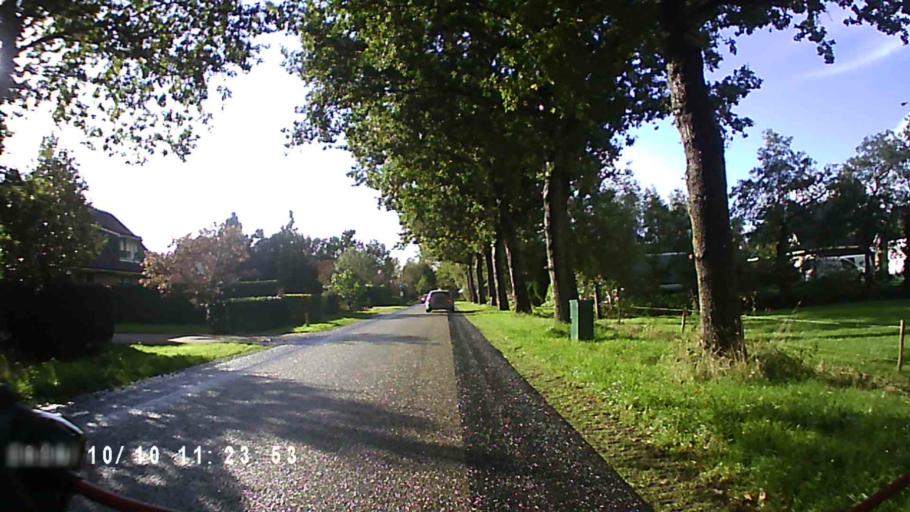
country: NL
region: Friesland
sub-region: Gemeente Smallingerland
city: Drachtstercompagnie
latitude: 53.0886
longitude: 6.1762
